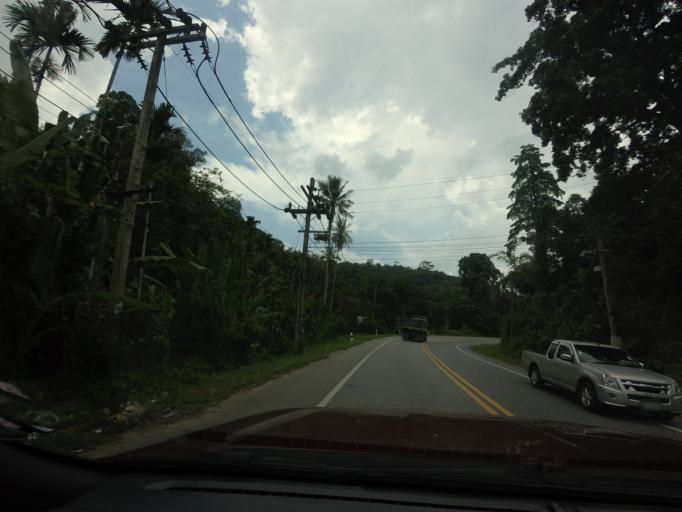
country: TH
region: Yala
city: Than To
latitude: 6.0785
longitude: 101.1871
